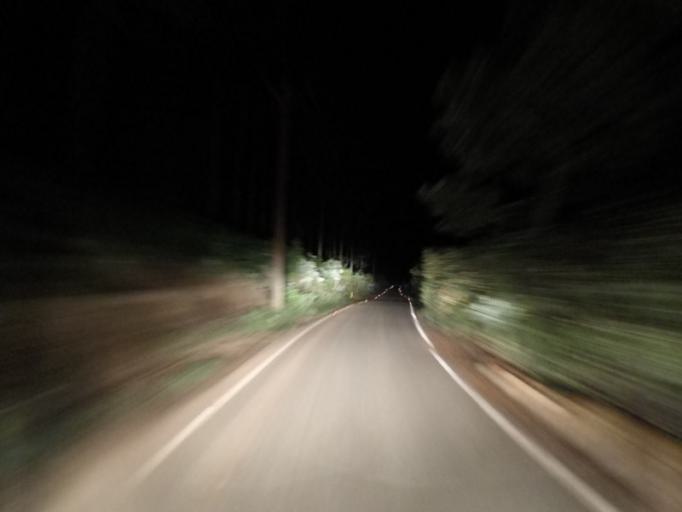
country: IN
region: Tamil Nadu
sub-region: Nilgiri
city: Kotagiri
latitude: 11.4721
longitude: 76.8846
